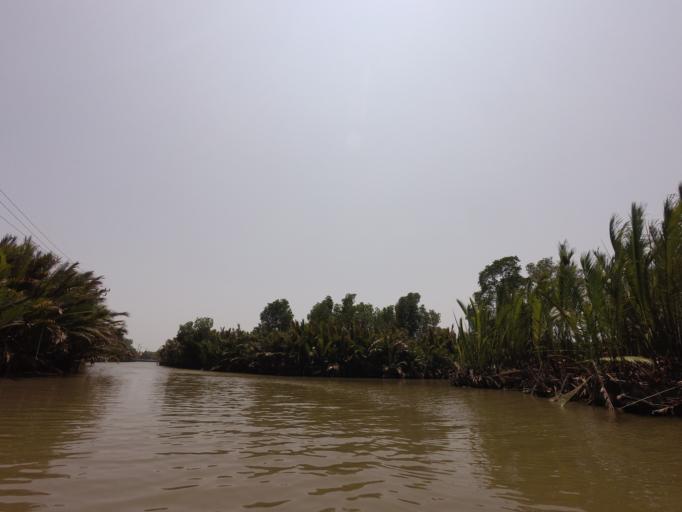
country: TH
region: Bangkok
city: Thung Khru
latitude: 13.5447
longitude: 100.4961
